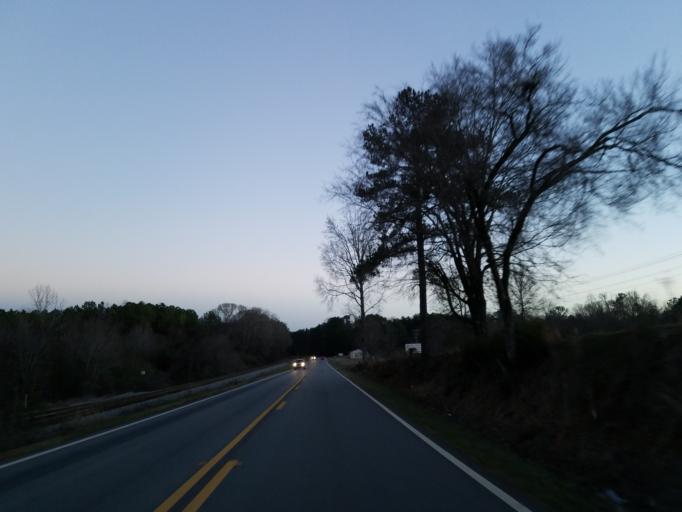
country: US
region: Georgia
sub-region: Monroe County
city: Forsyth
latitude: 32.9580
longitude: -83.8616
